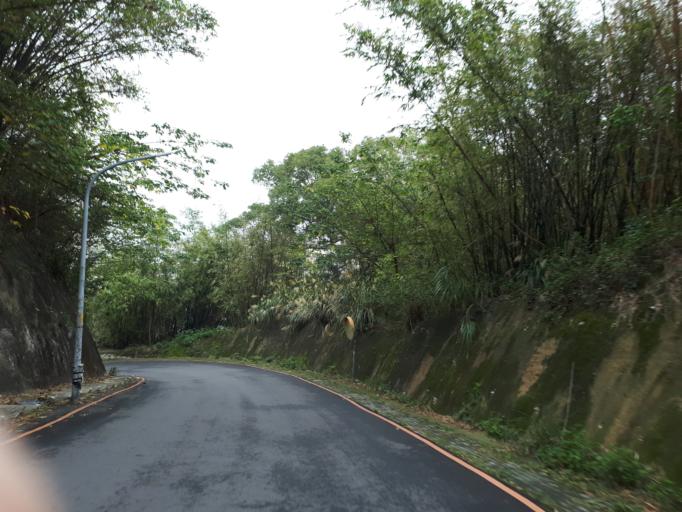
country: TW
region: Taiwan
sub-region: Hsinchu
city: Zhubei
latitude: 24.7390
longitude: 121.0840
